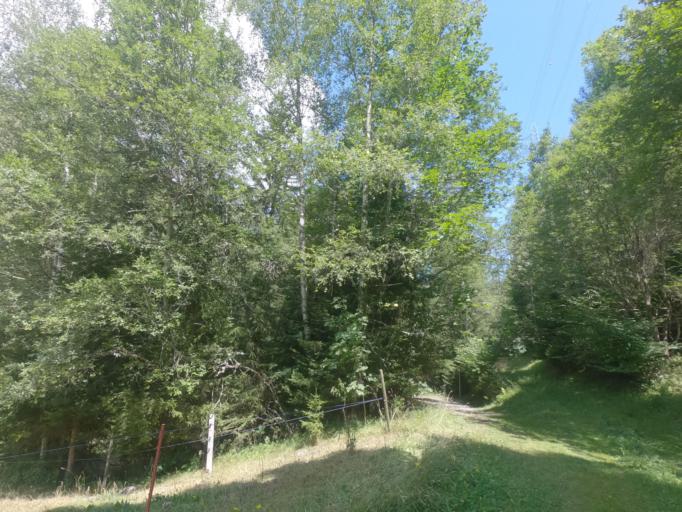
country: CH
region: Valais
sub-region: Saint-Maurice District
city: Salvan
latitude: 46.0693
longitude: 6.9693
